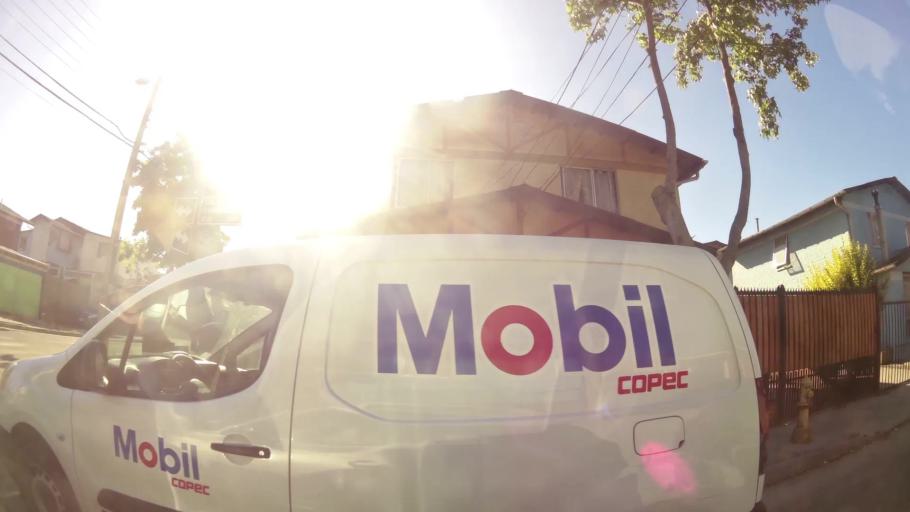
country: CL
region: Valparaiso
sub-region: Provincia de Valparaiso
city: Valparaiso
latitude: -33.1175
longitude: -71.5779
